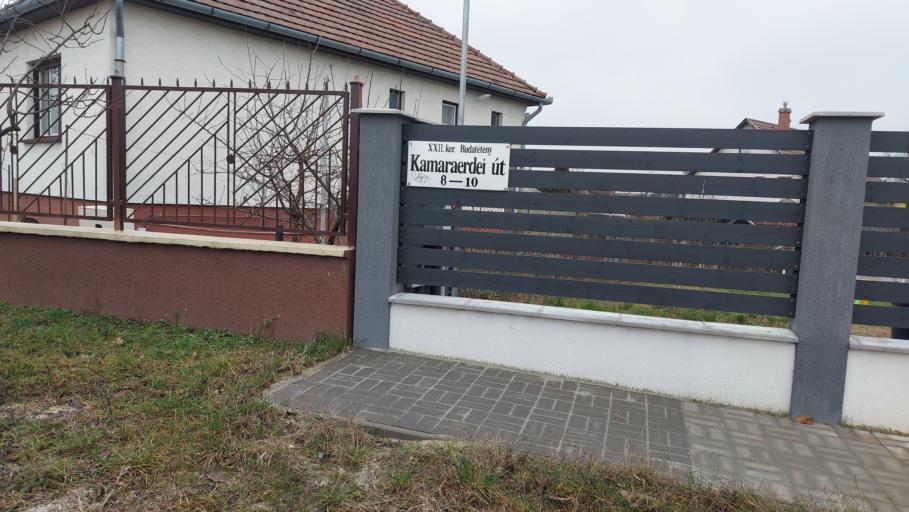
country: HU
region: Budapest
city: Budapest XXII. keruelet
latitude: 47.4317
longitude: 19.0025
